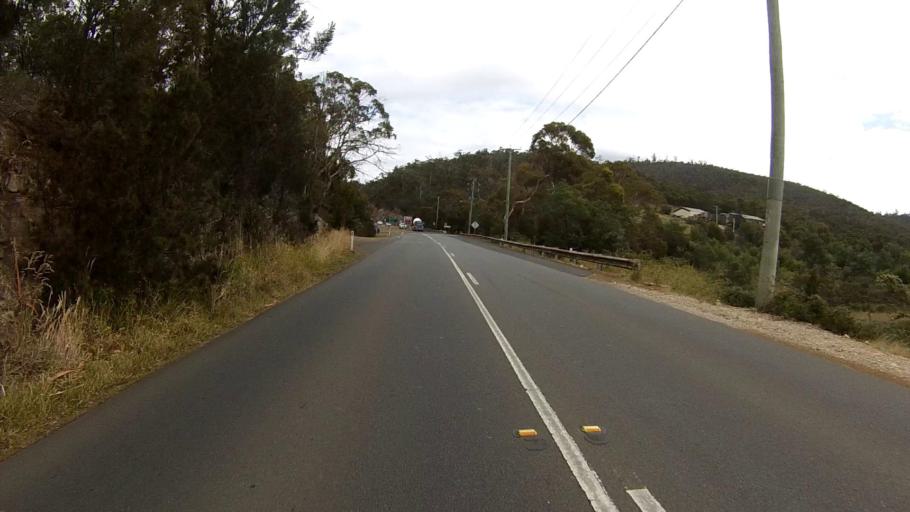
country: AU
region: Tasmania
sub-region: Clarence
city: Cambridge
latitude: -42.8436
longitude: 147.4204
